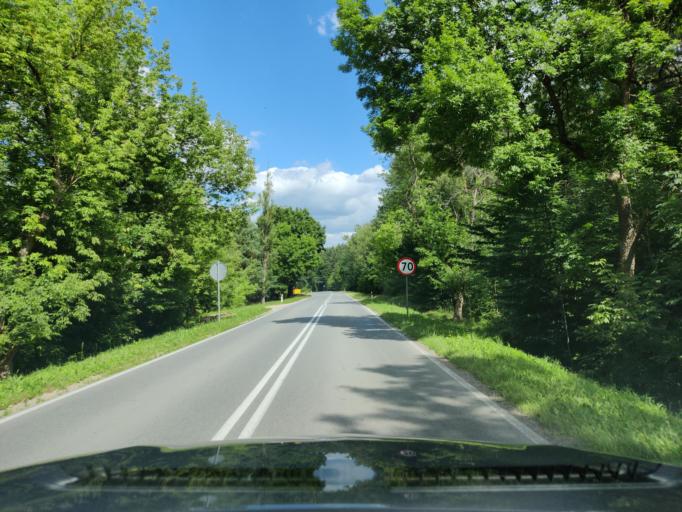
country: PL
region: Masovian Voivodeship
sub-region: Powiat wegrowski
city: Grebkow
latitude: 52.2221
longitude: 21.8746
